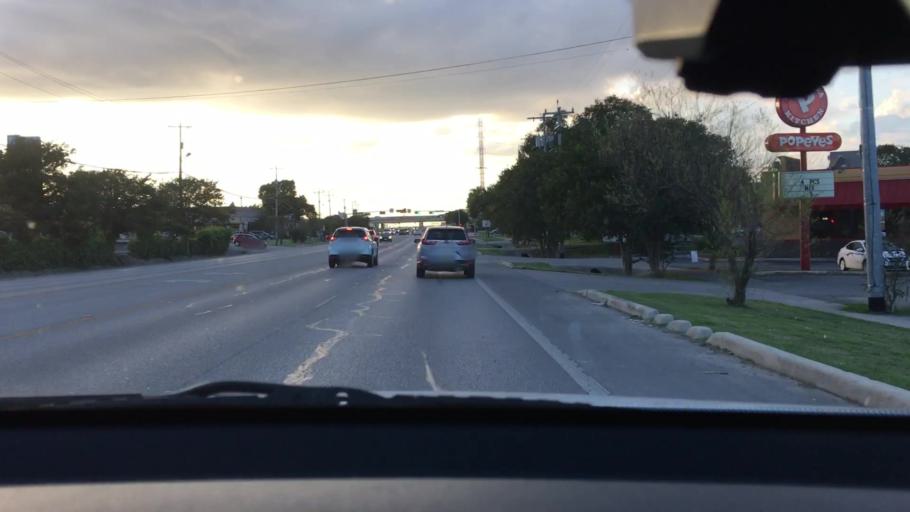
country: US
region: Texas
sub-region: Bexar County
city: Live Oak
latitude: 29.5587
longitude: -98.3227
